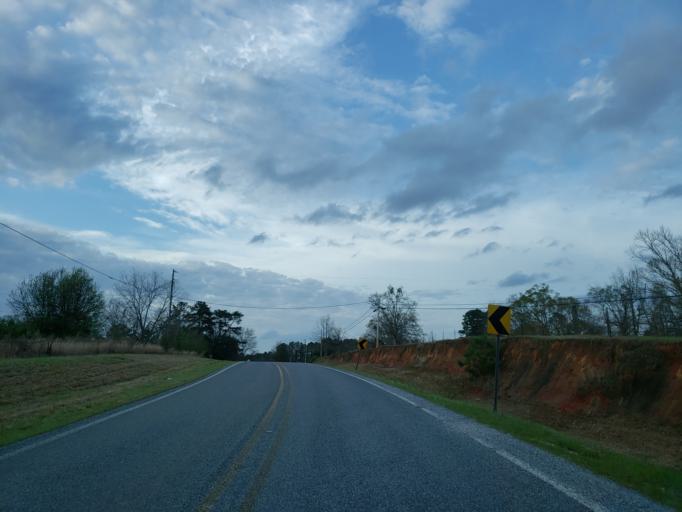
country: US
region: Mississippi
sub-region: Clarke County
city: Stonewall
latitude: 32.2165
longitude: -88.6986
